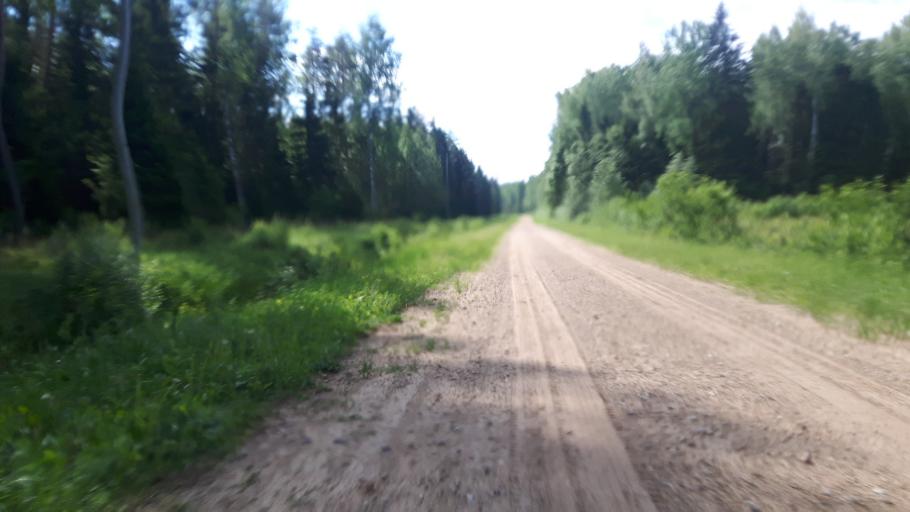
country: EE
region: Paernumaa
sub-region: Vaendra vald (alev)
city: Vandra
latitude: 58.7164
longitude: 25.0419
